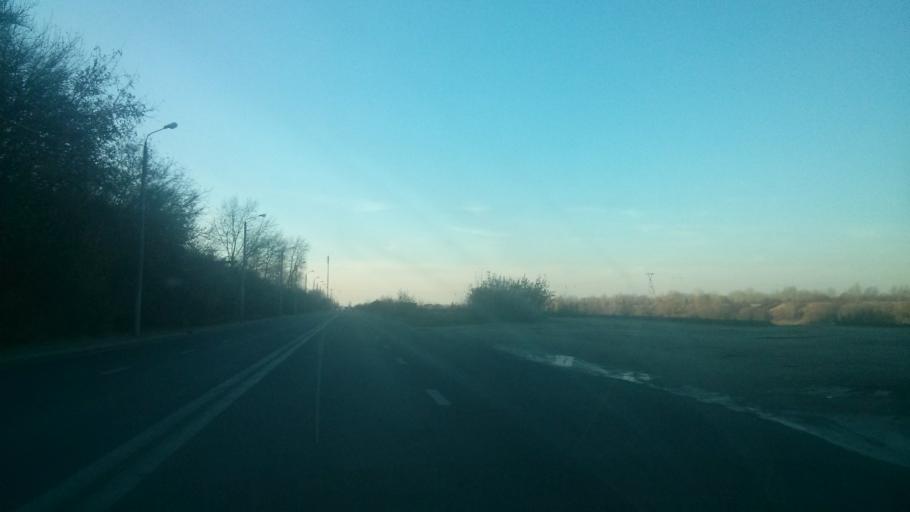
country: RU
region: Nizjnij Novgorod
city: Bor
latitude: 56.3200
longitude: 44.0722
